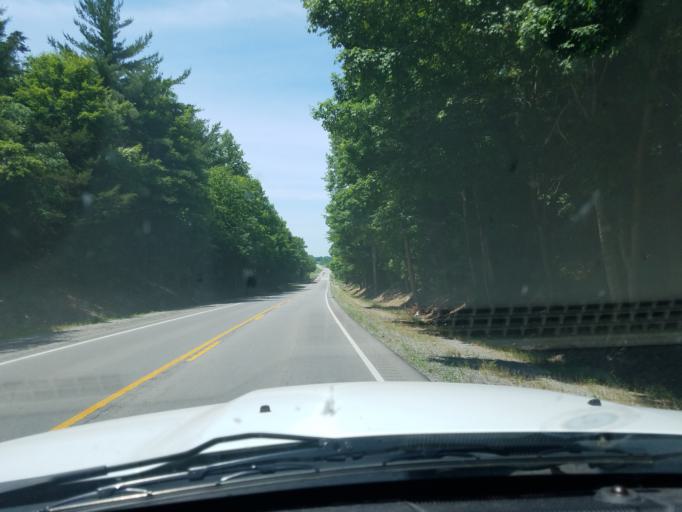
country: US
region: Kentucky
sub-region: Allen County
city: Scottsville
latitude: 36.6674
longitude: -86.2488
